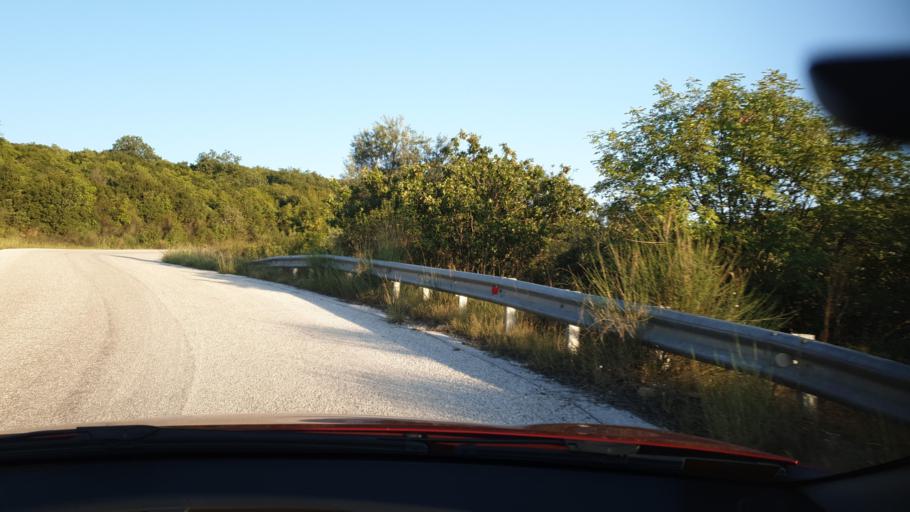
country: GR
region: Central Macedonia
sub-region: Nomos Chalkidikis
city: Galatista
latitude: 40.5561
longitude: 23.2841
